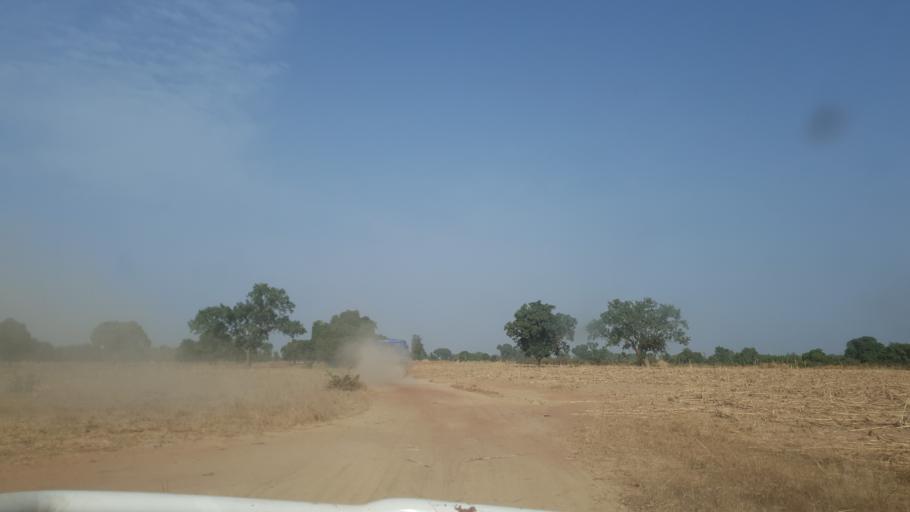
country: ML
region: Segou
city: Baroueli
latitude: 13.3508
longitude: -6.9413
